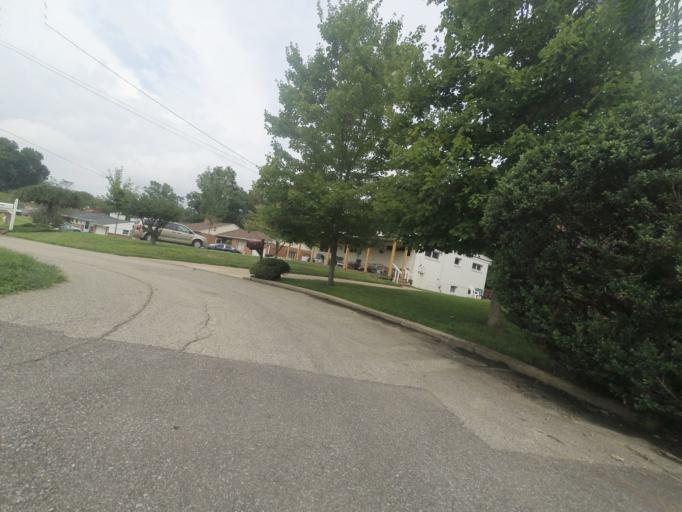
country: US
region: West Virginia
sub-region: Cabell County
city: Huntington
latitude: 38.3936
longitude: -82.4387
